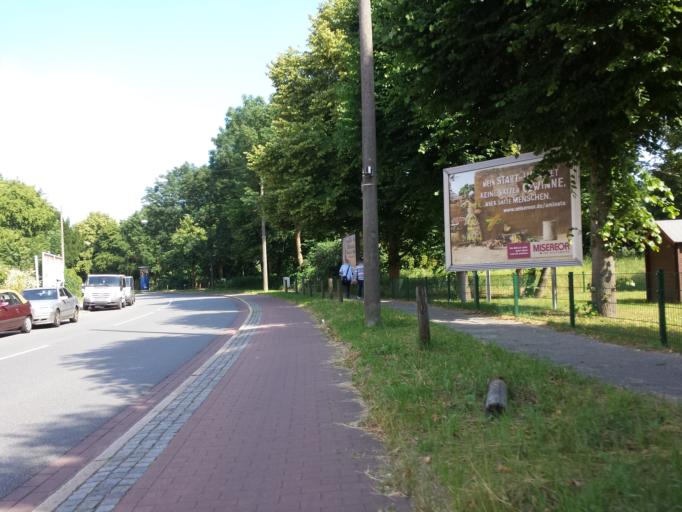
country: DE
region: Bremen
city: Bremen
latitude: 53.0883
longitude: 8.7555
